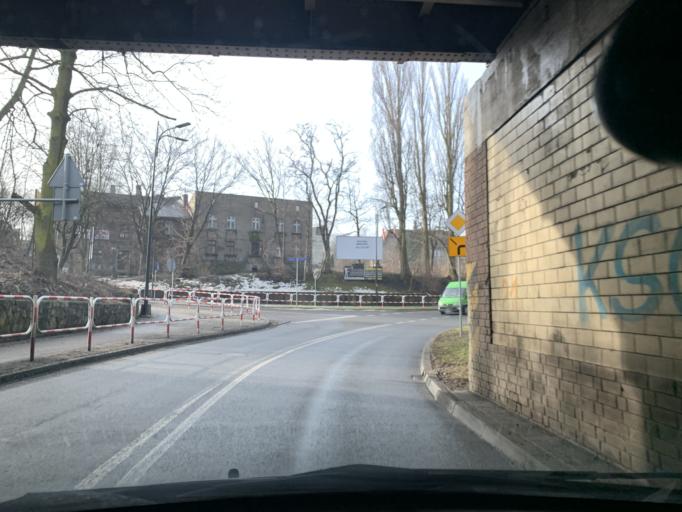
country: PL
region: Silesian Voivodeship
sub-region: Ruda Slaska
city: Ruda Slaska
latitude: 50.3150
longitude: 18.8567
